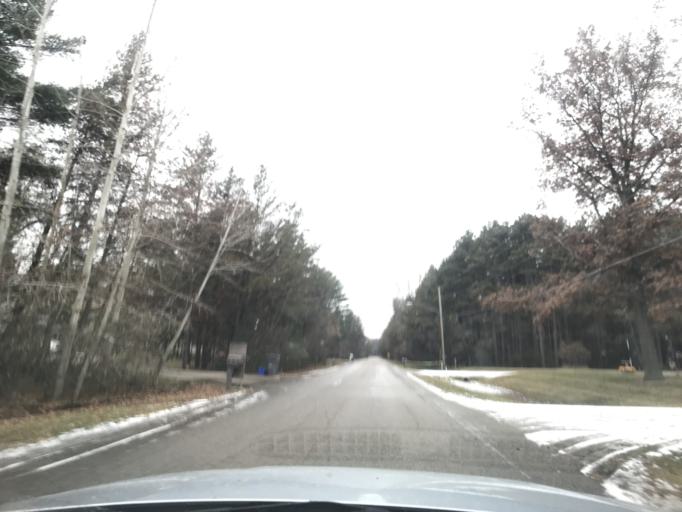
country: US
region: Wisconsin
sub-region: Marinette County
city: Marinette
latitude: 45.0483
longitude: -87.6273
